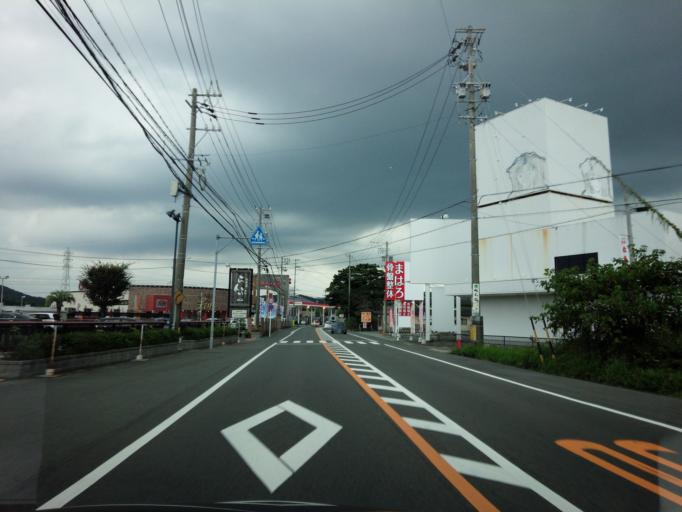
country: JP
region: Mie
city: Toba
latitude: 34.3450
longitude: 136.8146
